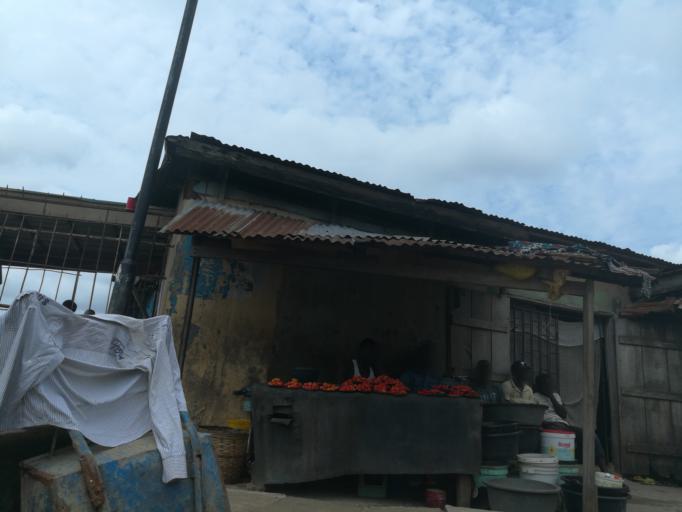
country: NG
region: Lagos
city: Somolu
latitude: 6.5459
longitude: 3.3948
